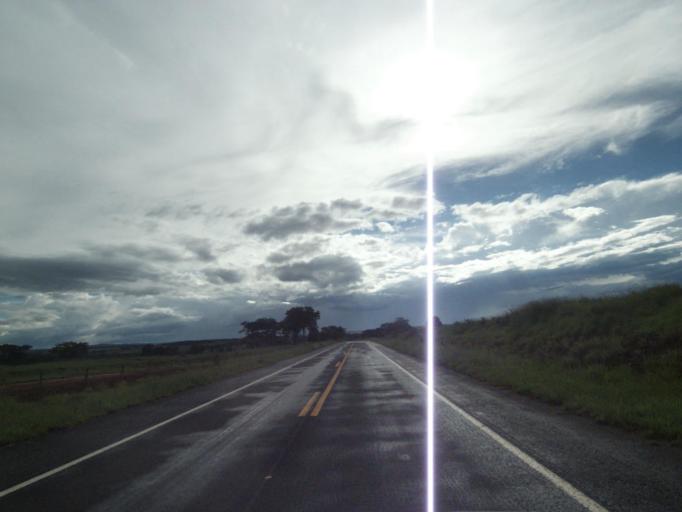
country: BR
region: Goias
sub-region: Itaberai
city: Itaberai
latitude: -15.9116
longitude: -49.5827
